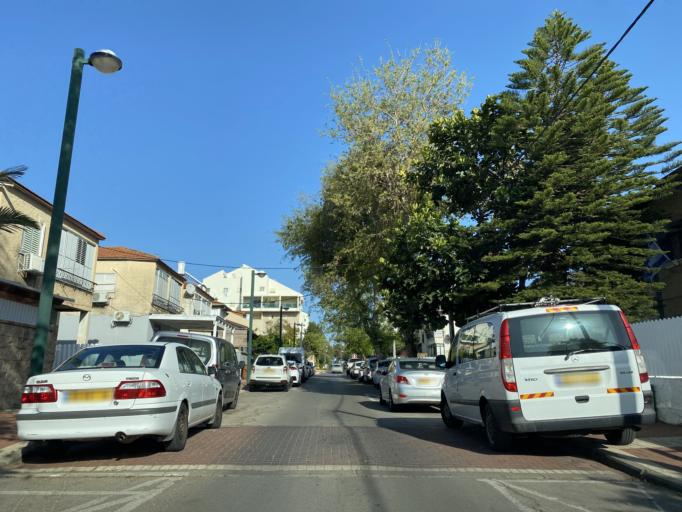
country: IL
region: Central District
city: Kfar Saba
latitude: 32.1808
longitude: 34.9180
